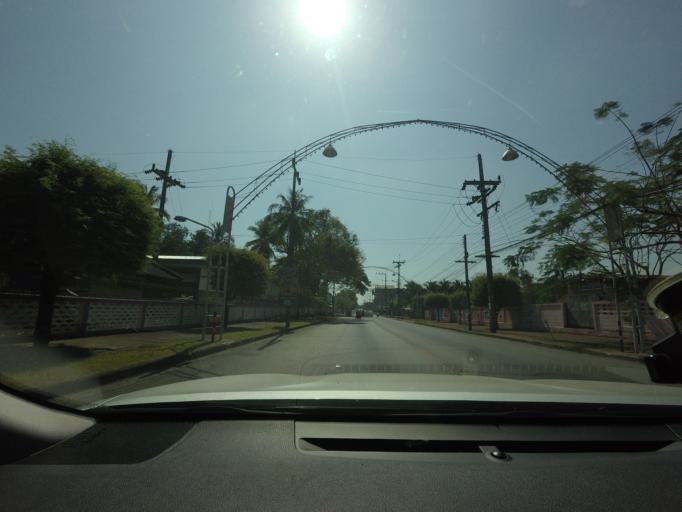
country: TH
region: Yala
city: Yala
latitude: 6.5470
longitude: 101.2860
